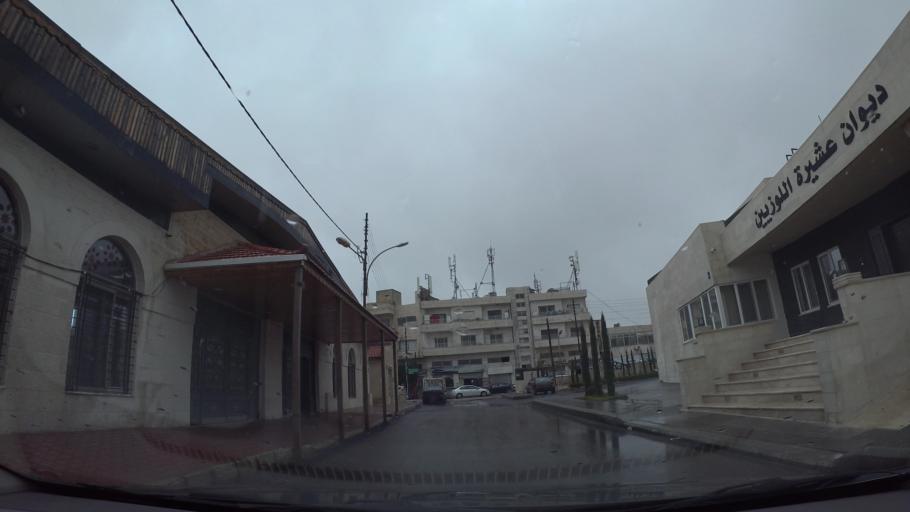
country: JO
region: Amman
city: Al Jubayhah
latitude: 32.0256
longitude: 35.8649
